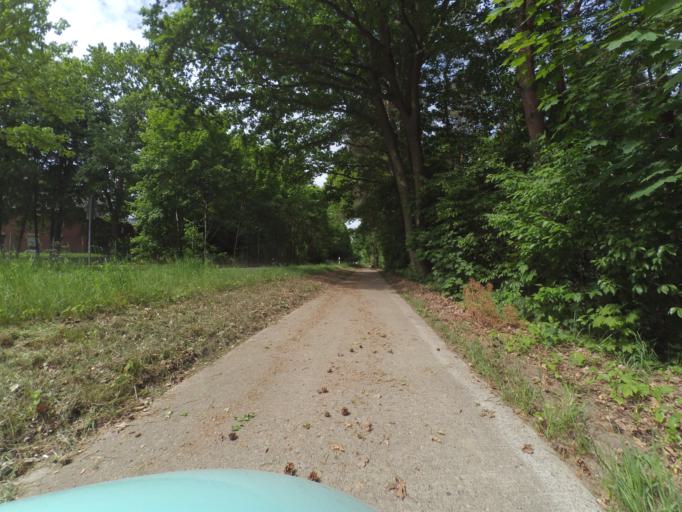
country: DE
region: Lower Saxony
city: Wunstorf
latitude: 52.4671
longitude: 9.4358
